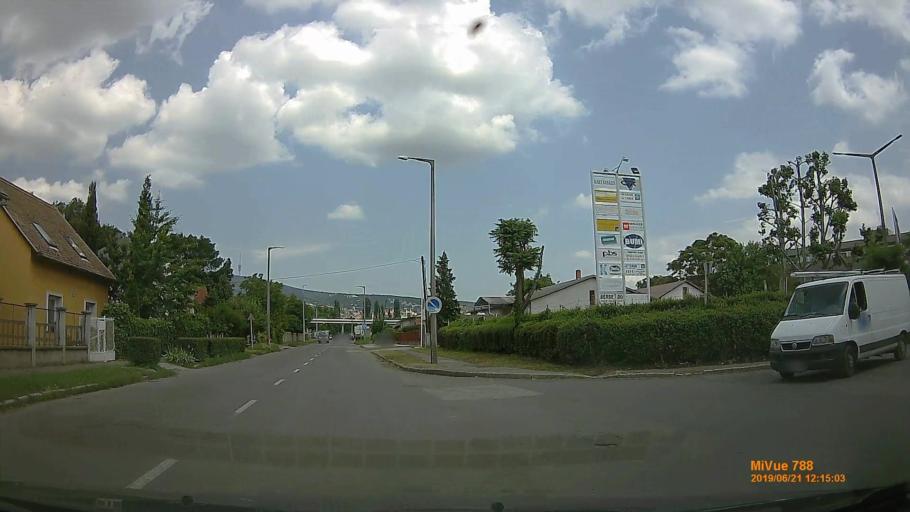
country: HU
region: Baranya
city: Pecs
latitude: 46.0610
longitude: 18.2128
